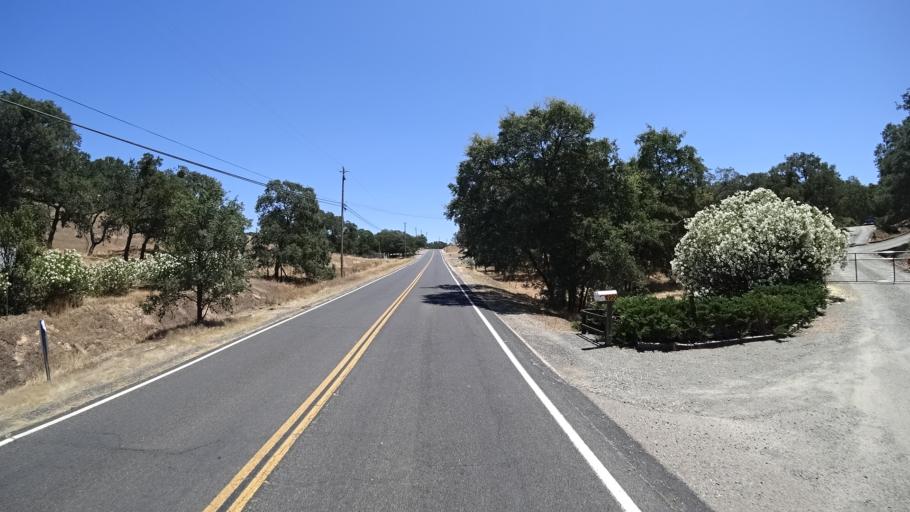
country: US
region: California
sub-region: Calaveras County
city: Rancho Calaveras
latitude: 38.1392
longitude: -120.8577
